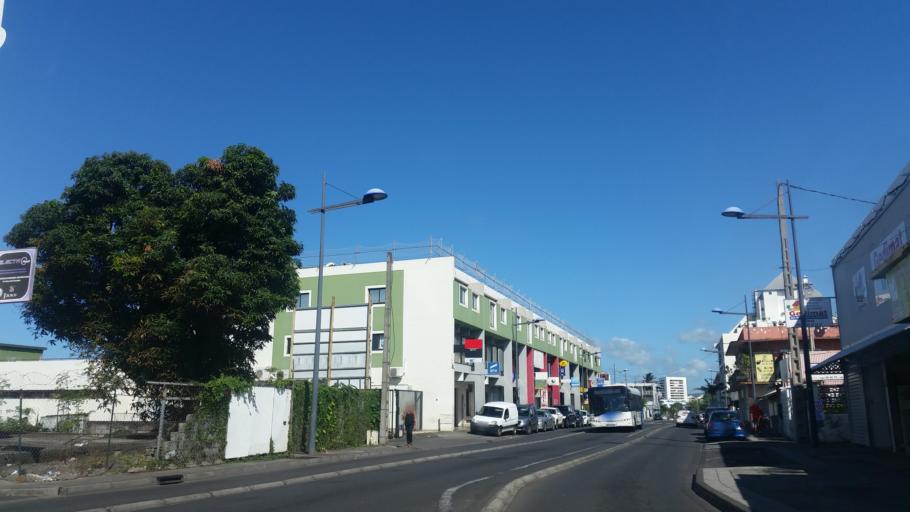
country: RE
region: Reunion
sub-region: Reunion
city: Saint-Denis
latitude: -20.8828
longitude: 55.4624
